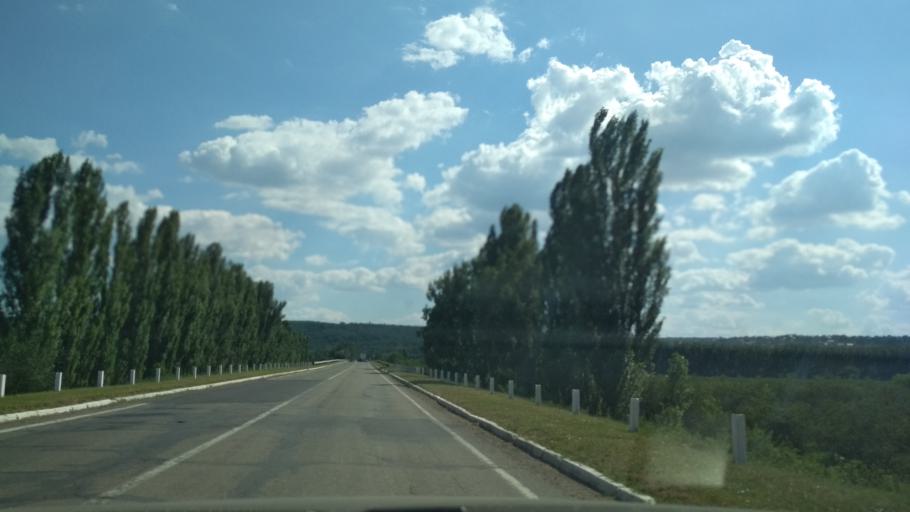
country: MD
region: Chisinau
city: Vadul lui Voda
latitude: 47.0950
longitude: 29.0949
